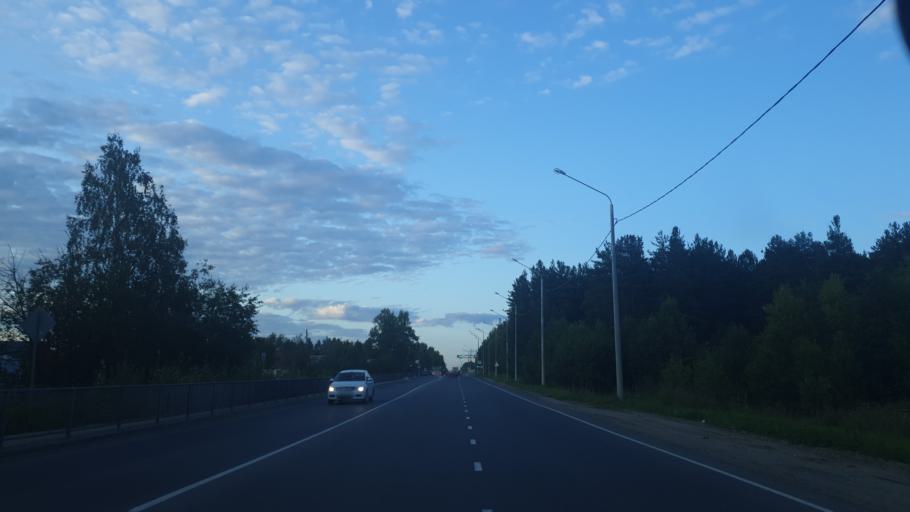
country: RU
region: Komi Republic
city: Verkhnyaya Maksakovka
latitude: 61.6648
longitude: 50.9707
